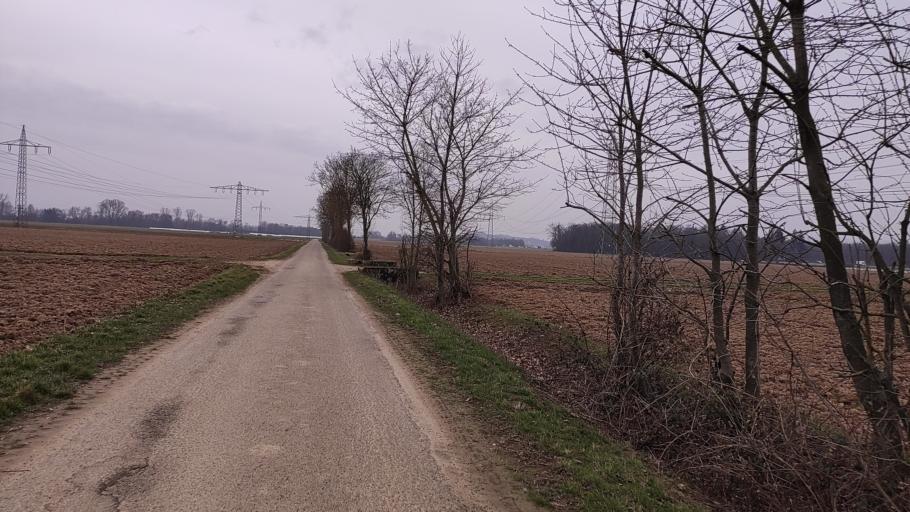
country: DE
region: Baden-Wuerttemberg
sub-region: Freiburg Region
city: Kenzingen
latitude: 48.1791
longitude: 7.7544
